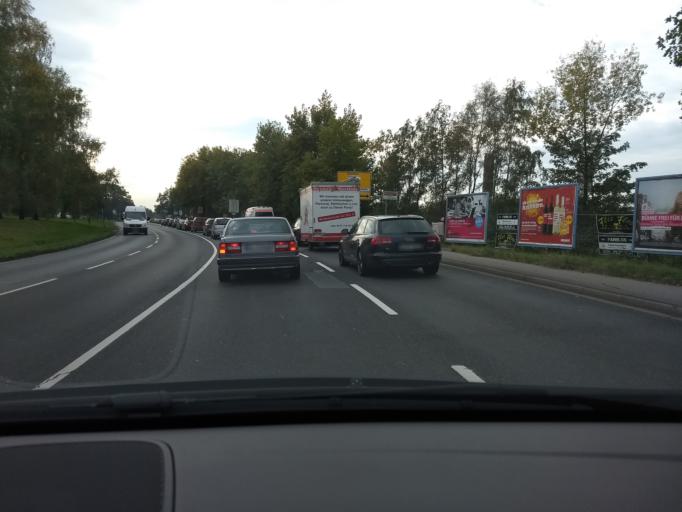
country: DE
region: North Rhine-Westphalia
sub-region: Regierungsbezirk Dusseldorf
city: Essen
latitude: 51.4969
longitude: 6.9955
